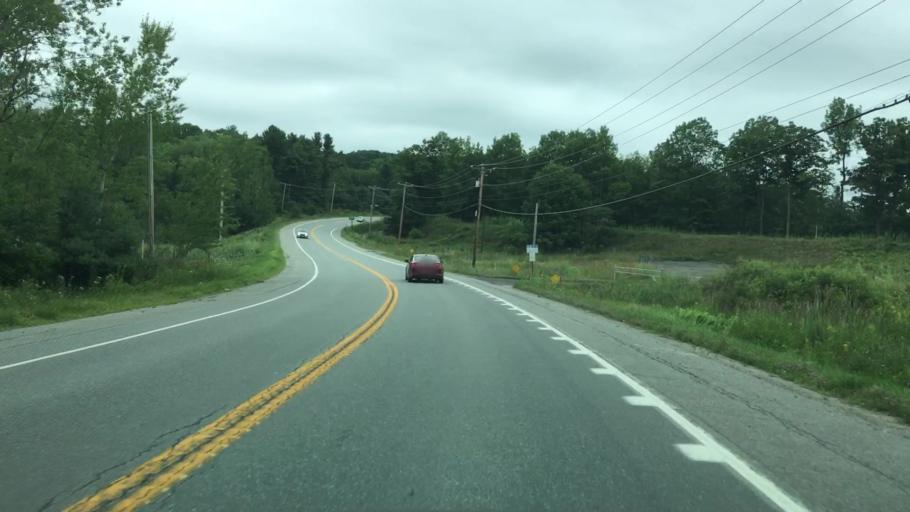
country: US
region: Maine
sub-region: Waldo County
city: Frankfort
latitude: 44.6244
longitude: -68.8689
